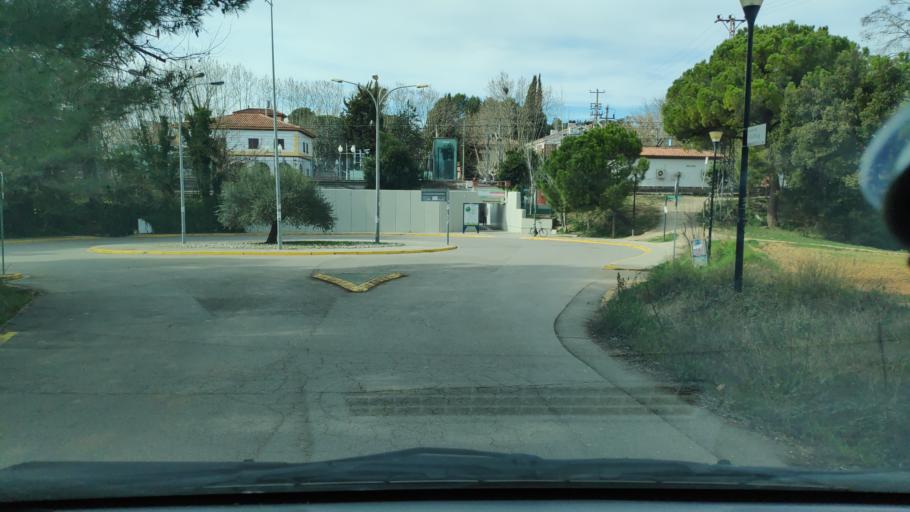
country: ES
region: Catalonia
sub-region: Provincia de Barcelona
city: Sant Quirze del Valles
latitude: 41.5007
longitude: 2.0915
